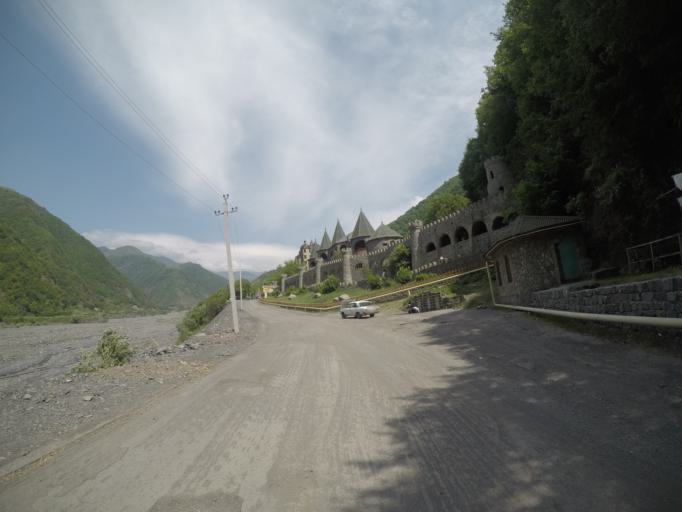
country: AZ
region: Qakh Rayon
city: Qaxbas
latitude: 41.4642
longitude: 47.0360
